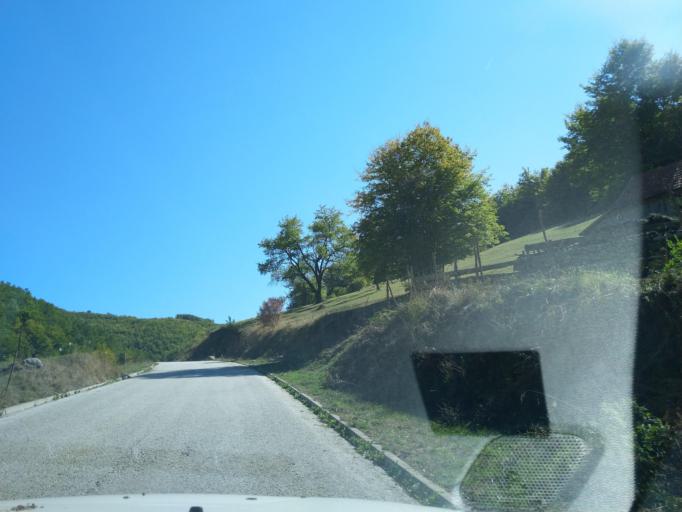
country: RS
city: Sokolovica
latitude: 43.2596
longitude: 20.2998
